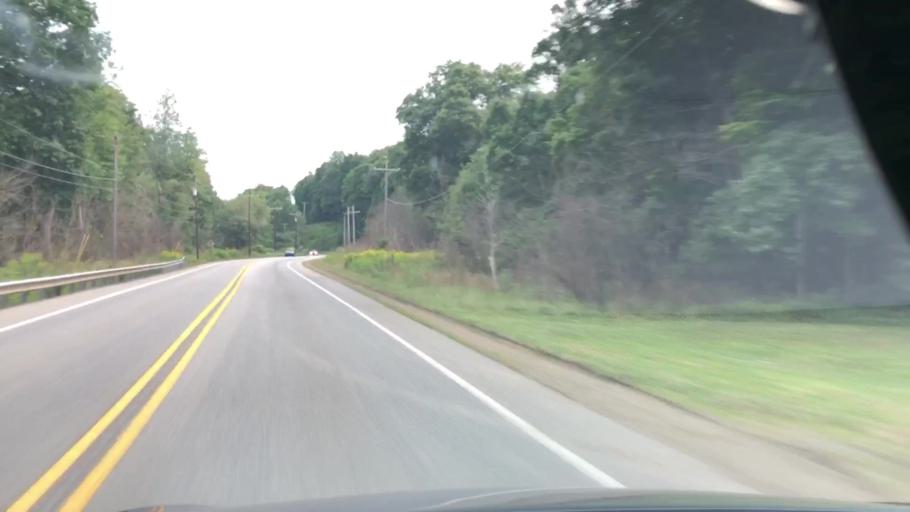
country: US
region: Pennsylvania
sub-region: Venango County
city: Hasson Heights
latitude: 41.4920
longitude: -79.7003
